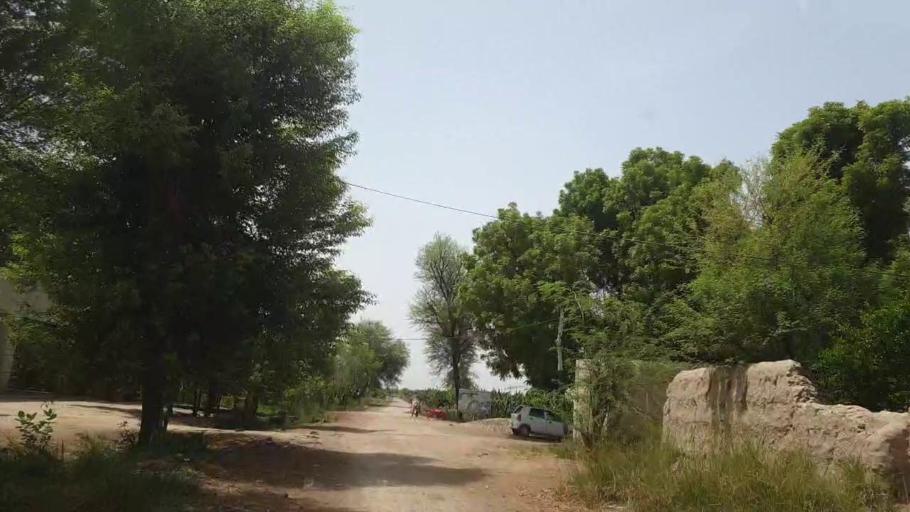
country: PK
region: Sindh
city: Sakrand
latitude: 26.0723
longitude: 68.2667
